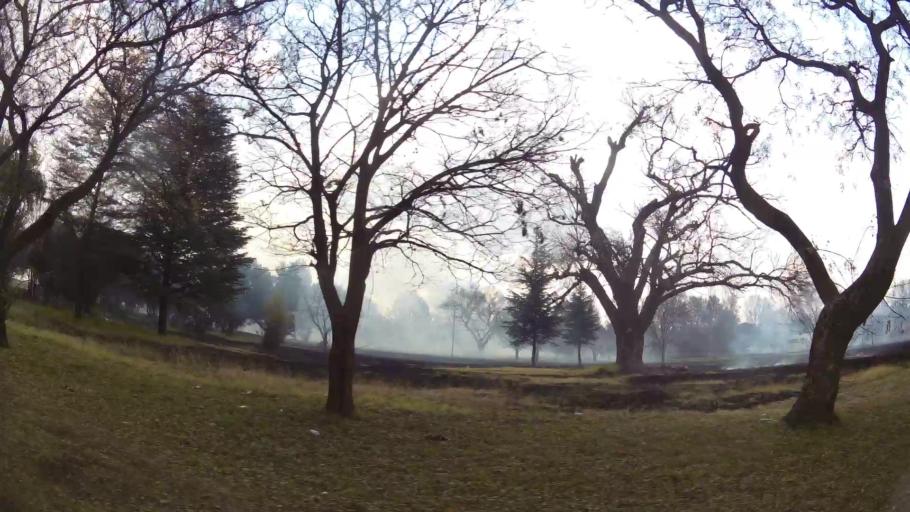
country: ZA
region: Mpumalanga
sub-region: Nkangala District Municipality
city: Delmas
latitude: -26.1447
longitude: 28.6719
